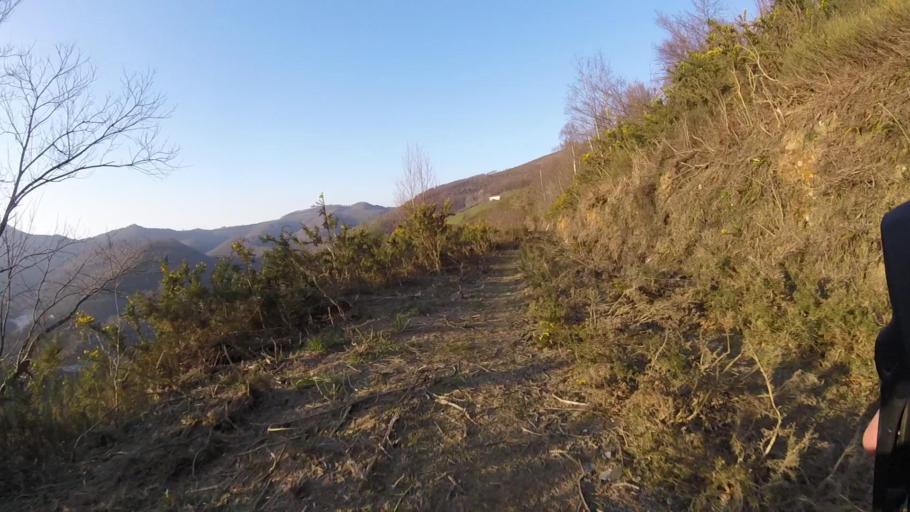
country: ES
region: Navarre
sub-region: Provincia de Navarra
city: Arano
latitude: 43.2263
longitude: -1.8625
